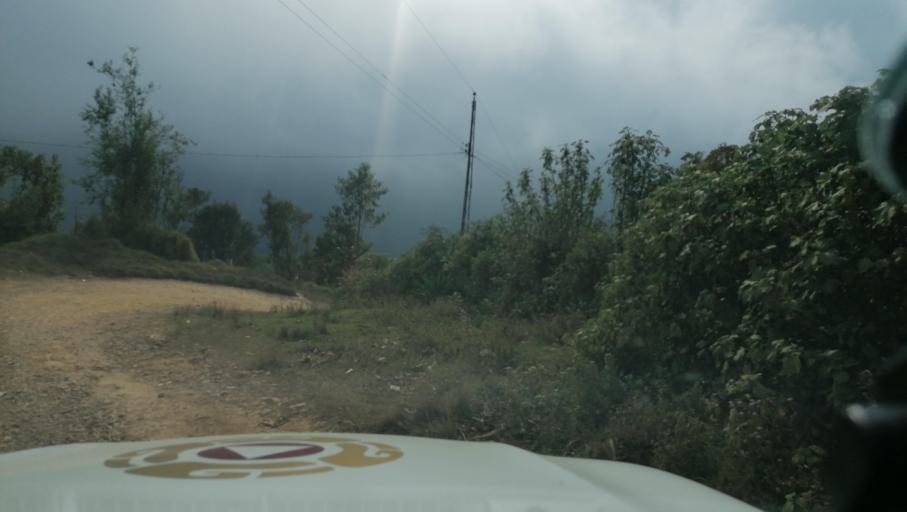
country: GT
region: San Marcos
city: Tacana
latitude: 15.2183
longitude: -92.1919
